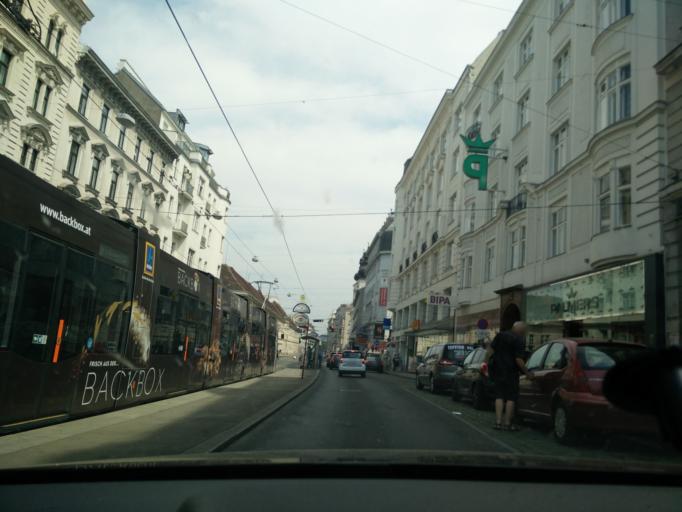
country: AT
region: Vienna
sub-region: Wien Stadt
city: Vienna
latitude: 48.2150
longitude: 16.3498
